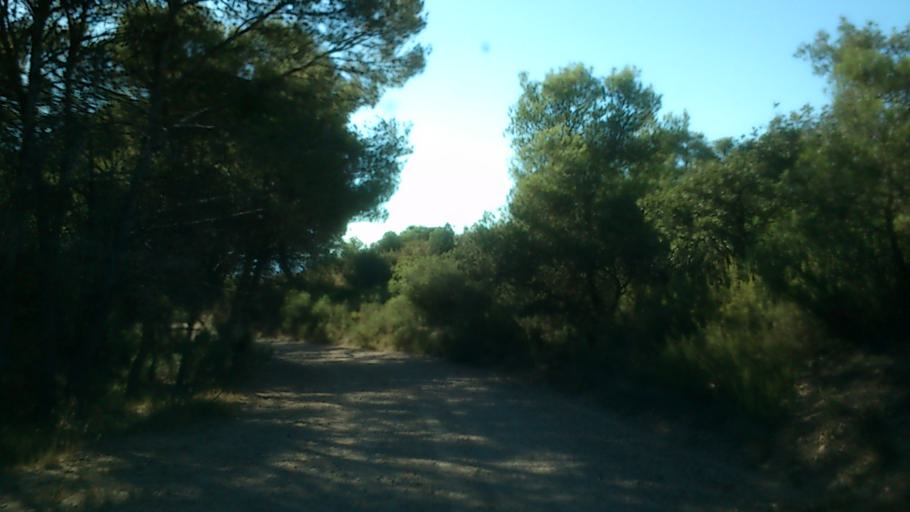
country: ES
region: Aragon
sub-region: Provincia de Zaragoza
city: San Mateo de Gallego
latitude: 41.7737
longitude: -0.7166
